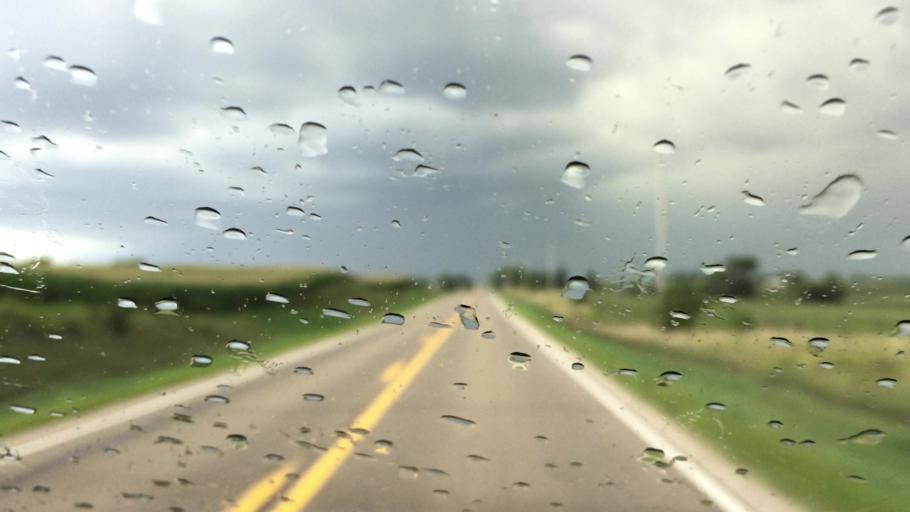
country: US
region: Iowa
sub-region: Henry County
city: Mount Pleasant
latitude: 40.7843
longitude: -91.5306
